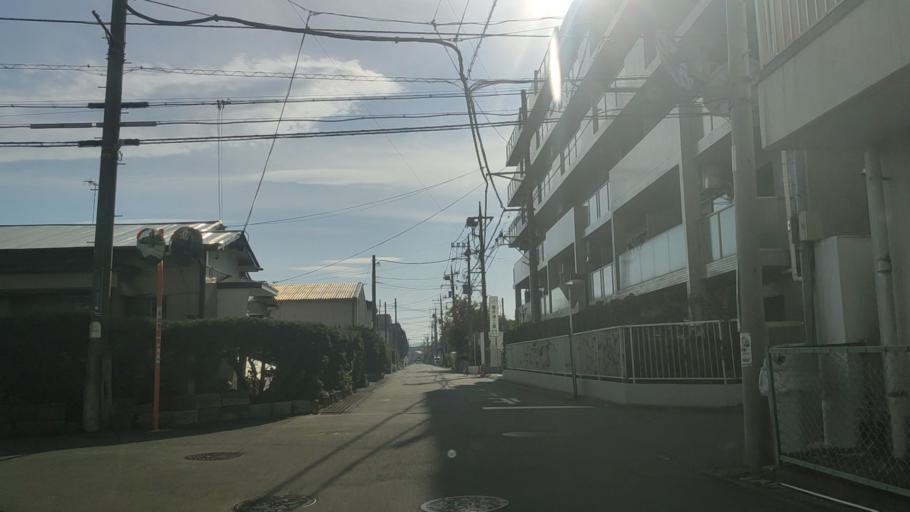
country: JP
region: Kanagawa
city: Atsugi
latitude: 35.4287
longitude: 139.3671
